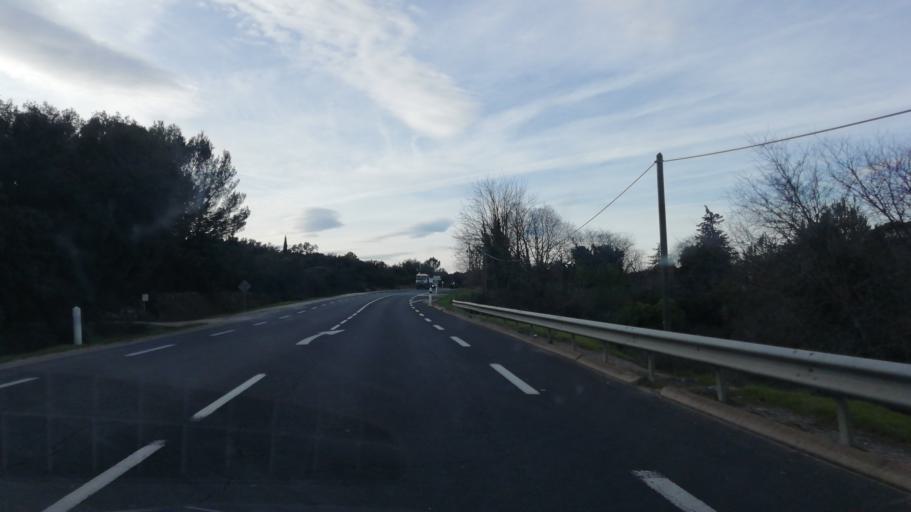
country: FR
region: Languedoc-Roussillon
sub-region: Departement du Gard
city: Caveirac
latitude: 43.8512
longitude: 4.2759
